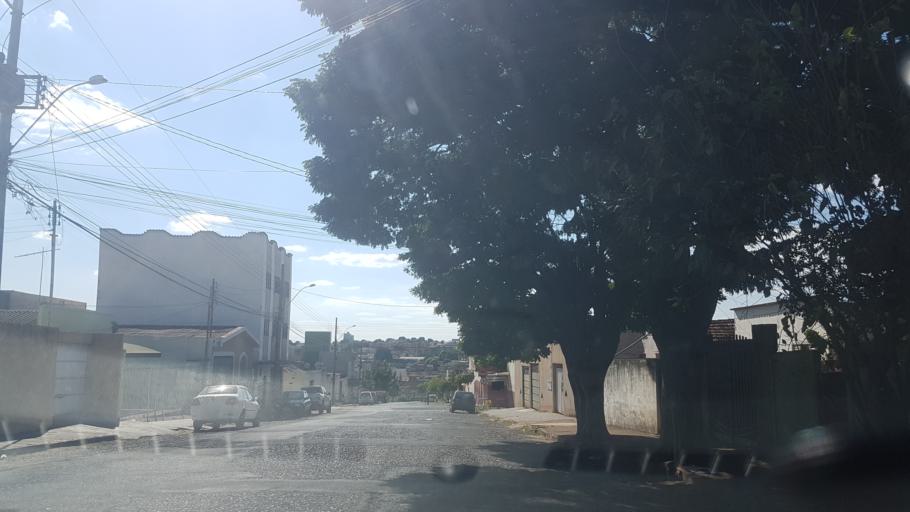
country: BR
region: Minas Gerais
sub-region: Uberlandia
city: Uberlandia
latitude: -18.9088
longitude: -48.2902
